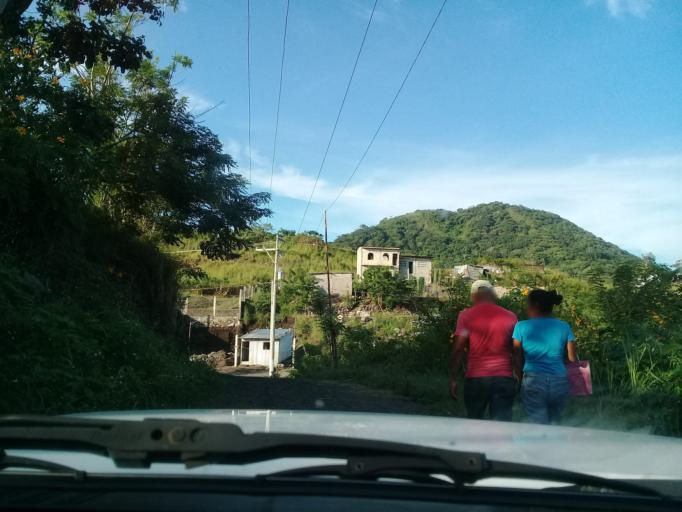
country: MX
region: Veracruz
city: Catemaco
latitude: 18.4252
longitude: -95.1021
